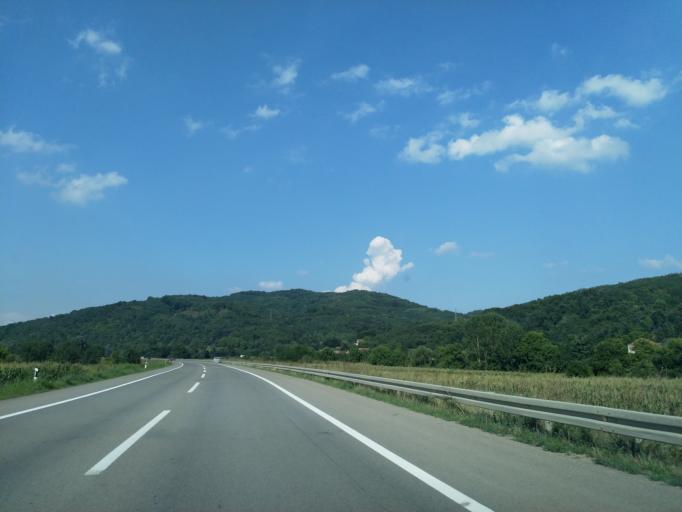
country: RS
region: Central Serbia
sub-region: Rasinski Okrug
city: Krusevac
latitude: 43.6203
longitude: 21.3699
